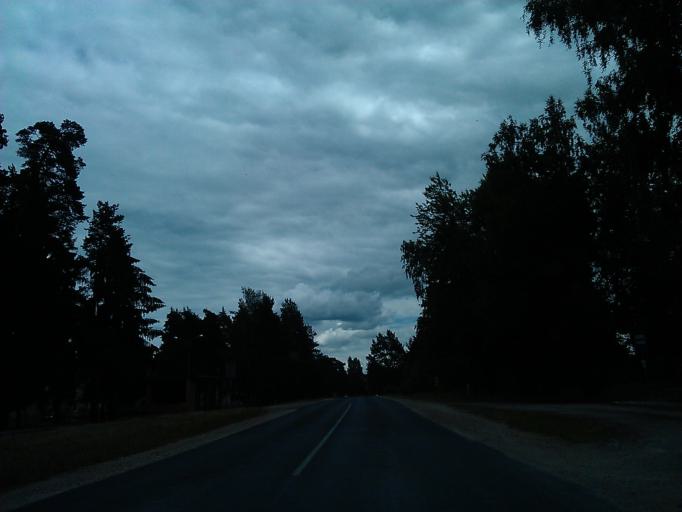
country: LV
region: Dobeles Rajons
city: Dobele
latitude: 56.6489
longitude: 23.2161
